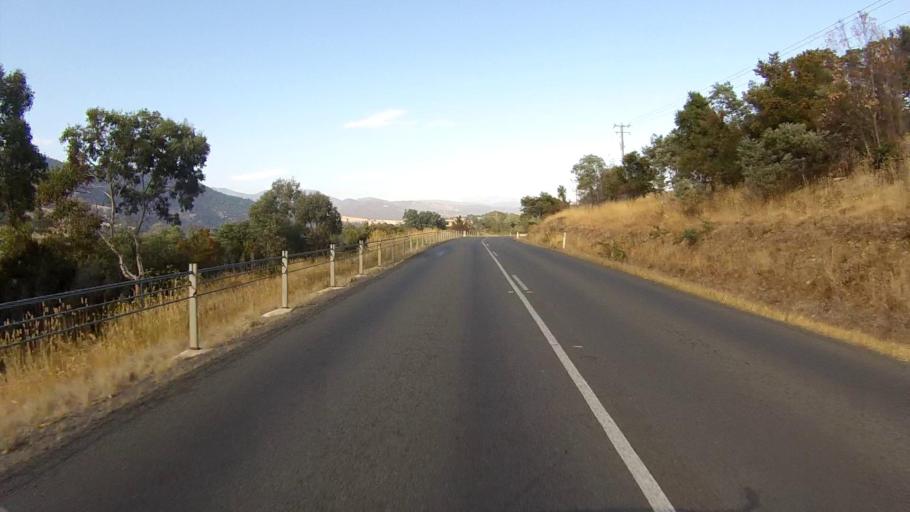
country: AU
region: Tasmania
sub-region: Glenorchy
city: Granton
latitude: -42.7536
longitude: 147.1468
